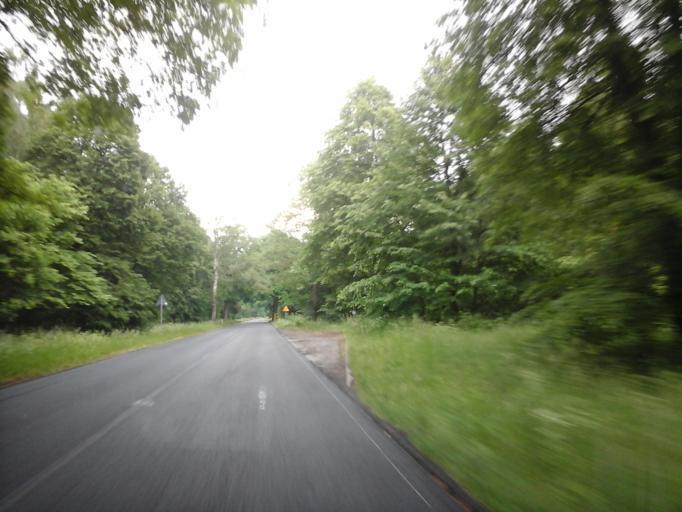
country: PL
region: West Pomeranian Voivodeship
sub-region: Powiat choszczenski
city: Recz
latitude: 53.1917
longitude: 15.6415
